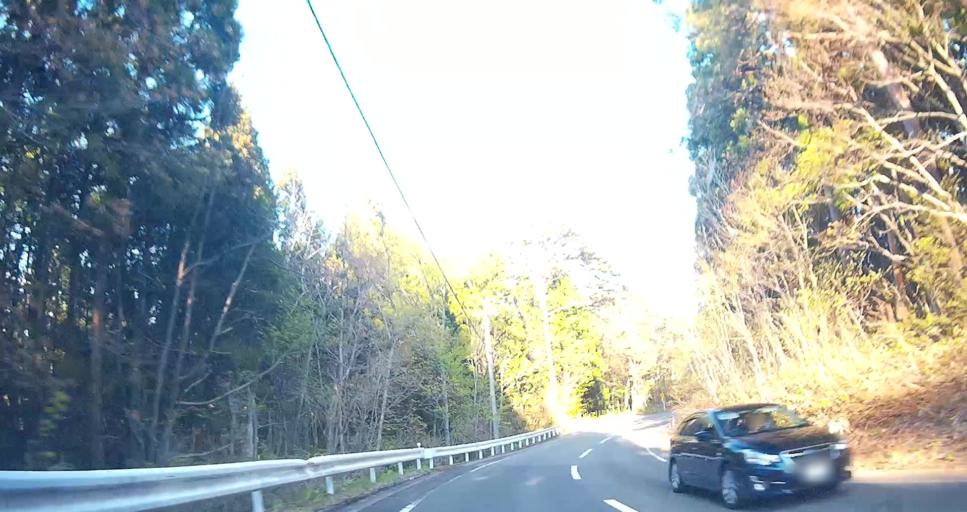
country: JP
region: Aomori
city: Mutsu
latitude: 41.3199
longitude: 141.1412
